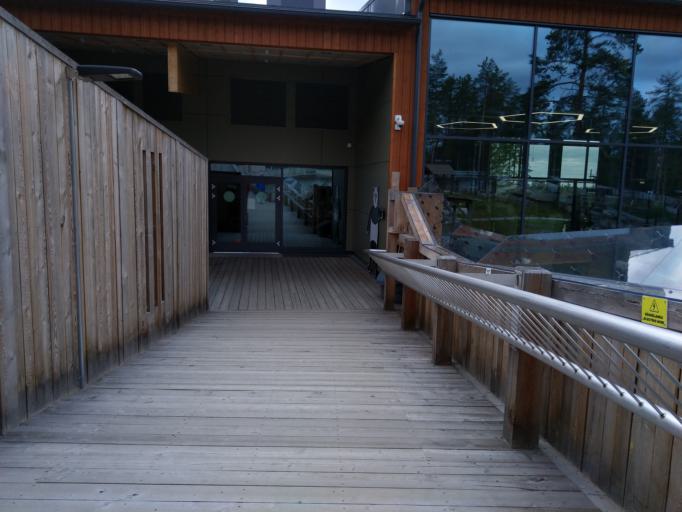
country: FI
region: Southern Ostrobothnia
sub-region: Kuusiokunnat
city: AEhtaeri
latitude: 62.5369
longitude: 24.1840
